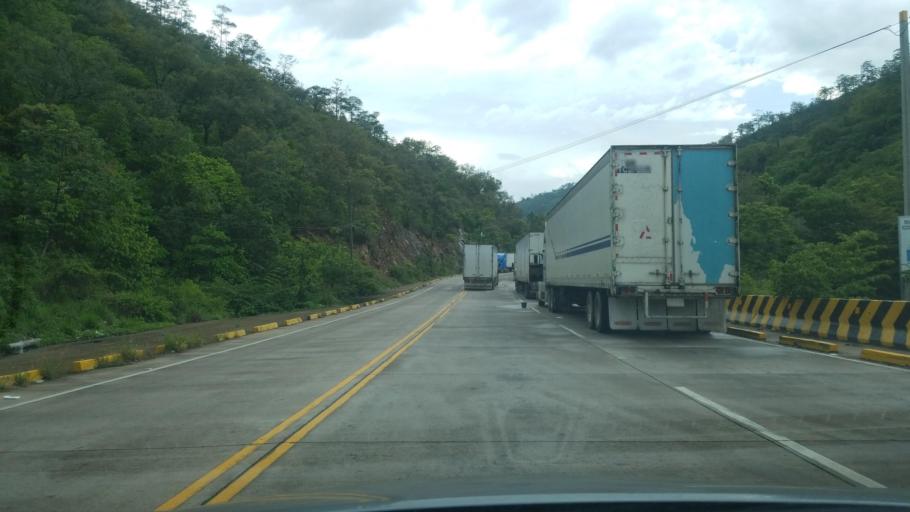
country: HN
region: Copan
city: Copan
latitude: 14.8572
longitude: -89.2192
